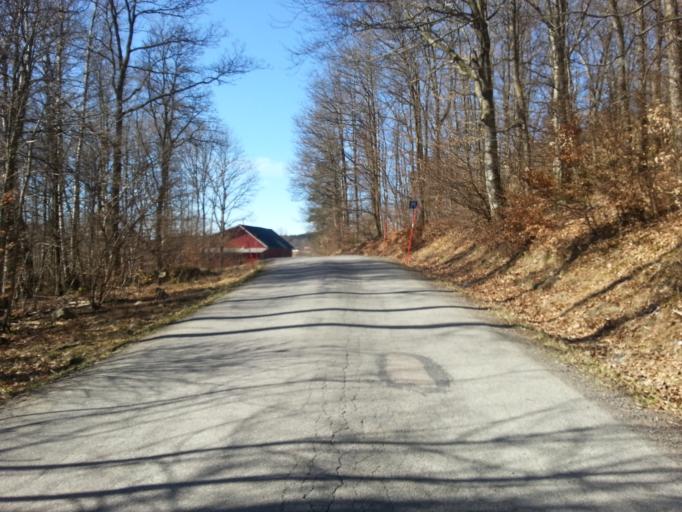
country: SE
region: Vaestra Goetaland
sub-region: Kungalvs Kommun
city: Kungalv
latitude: 57.9008
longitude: 11.9656
